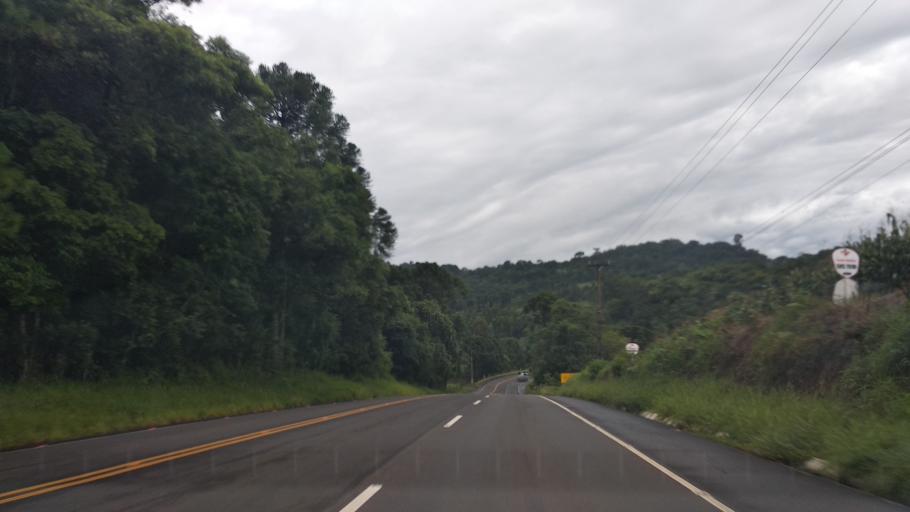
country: BR
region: Santa Catarina
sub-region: Videira
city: Videira
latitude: -27.0507
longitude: -51.1712
